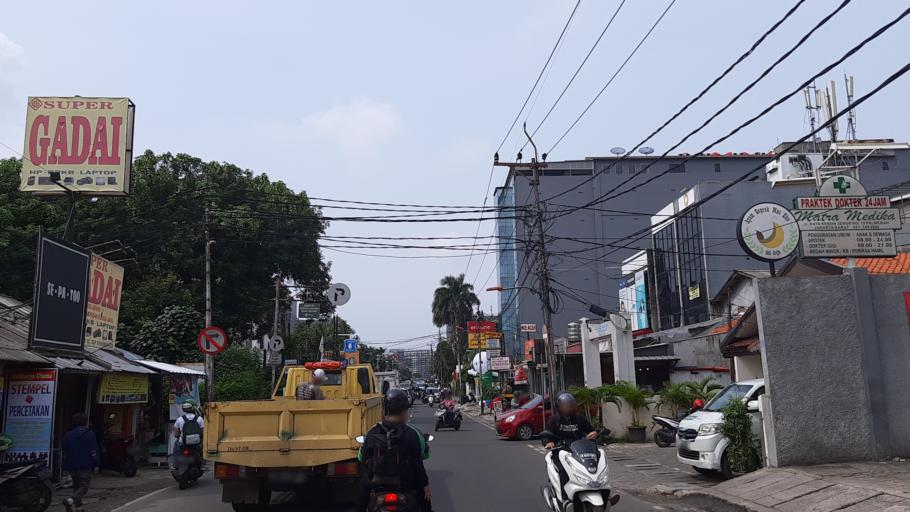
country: ID
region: Jakarta Raya
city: Jakarta
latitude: -6.2029
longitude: 106.7828
